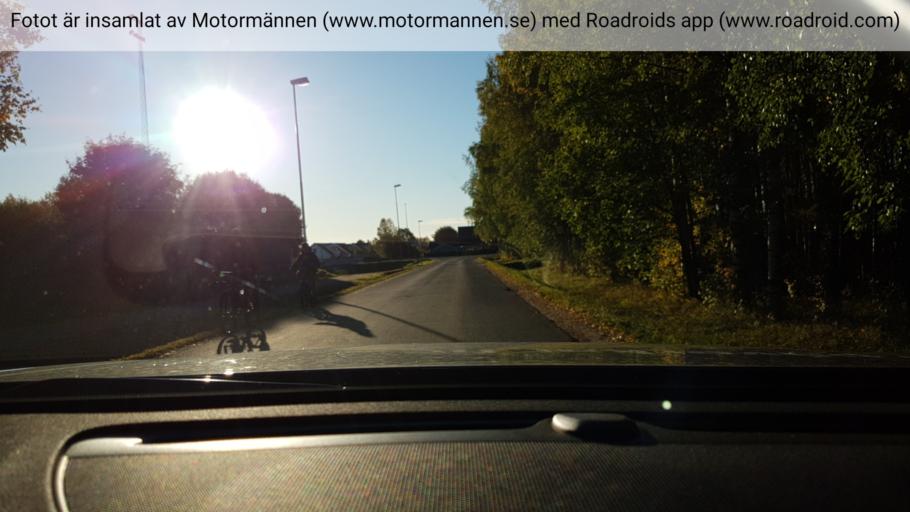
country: SE
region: Norrbotten
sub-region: Lulea Kommun
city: Sodra Sunderbyn
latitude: 65.6588
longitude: 21.9487
